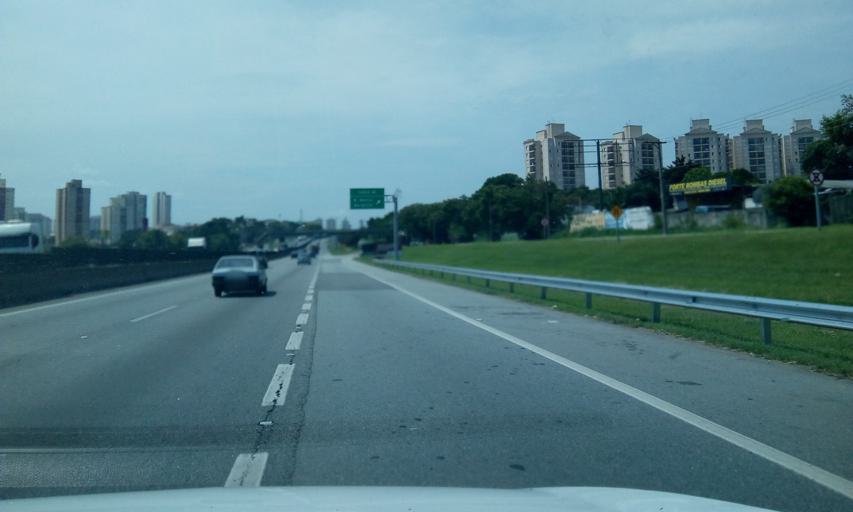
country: BR
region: Sao Paulo
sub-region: Jundiai
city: Jundiai
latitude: -23.1756
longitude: -46.9184
